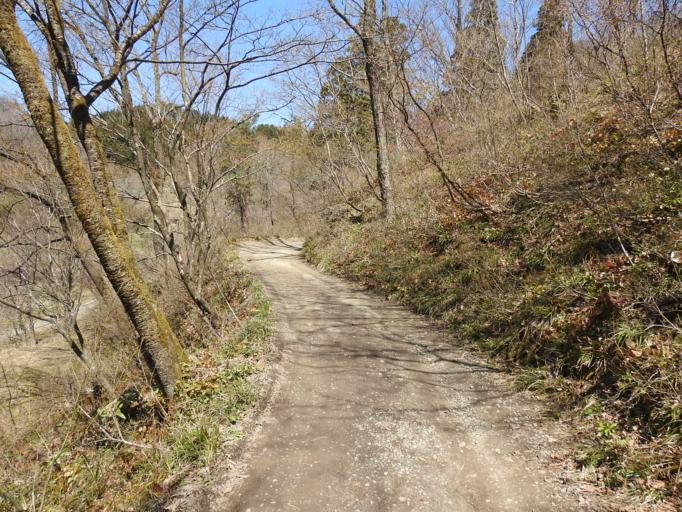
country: JP
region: Niigata
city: Nagaoka
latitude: 37.4625
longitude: 138.7455
